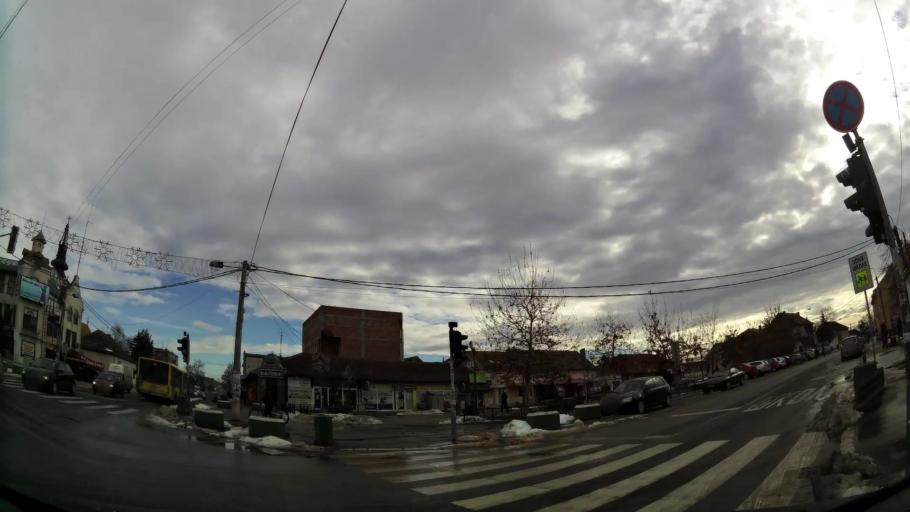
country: RS
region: Central Serbia
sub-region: Belgrade
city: Surcin
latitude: 44.7910
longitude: 20.2701
